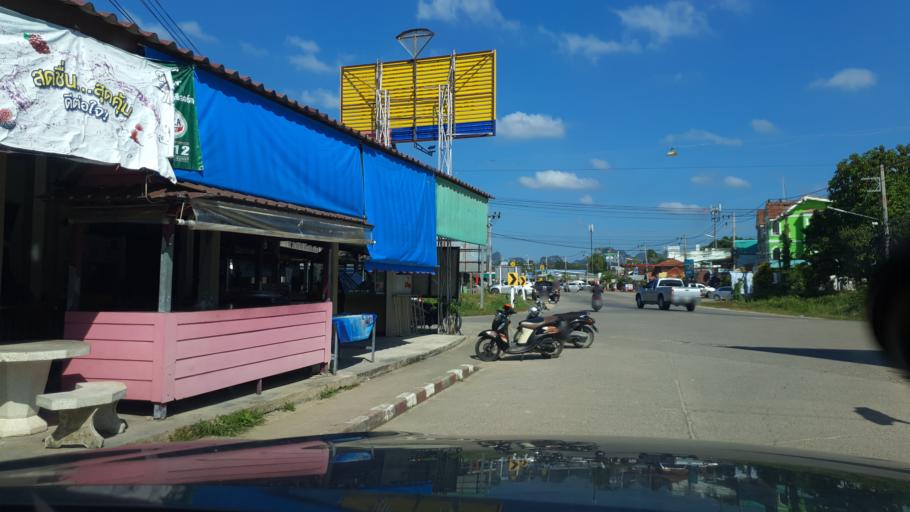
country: TH
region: Phangnga
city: Ban Ao Nang
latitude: 8.0303
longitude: 98.8629
